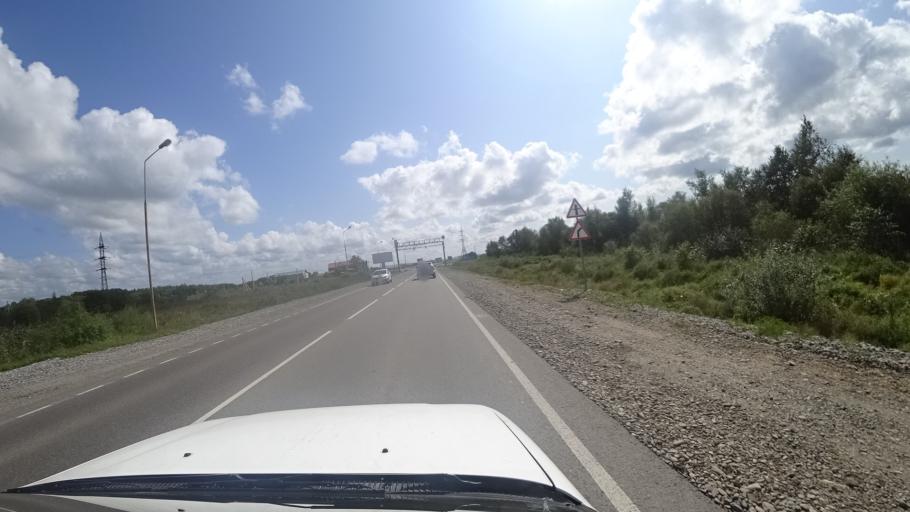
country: RU
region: Primorskiy
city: Dal'nerechensk
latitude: 45.9196
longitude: 133.7725
